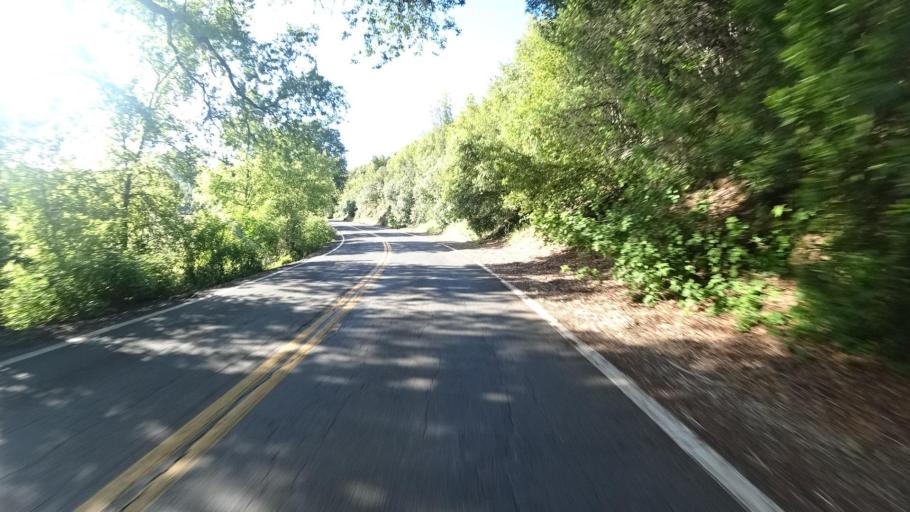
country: US
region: California
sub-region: Lake County
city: North Lakeport
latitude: 39.0925
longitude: -122.9591
